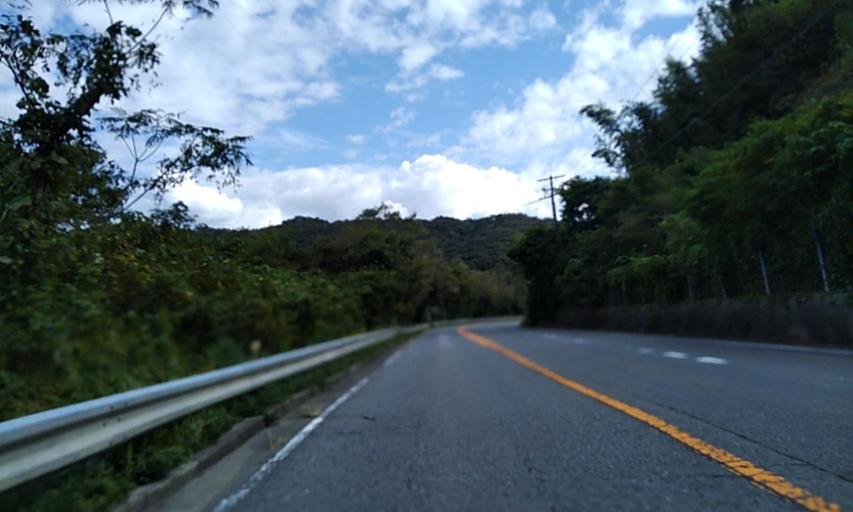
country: JP
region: Wakayama
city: Gobo
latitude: 33.9416
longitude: 135.1325
